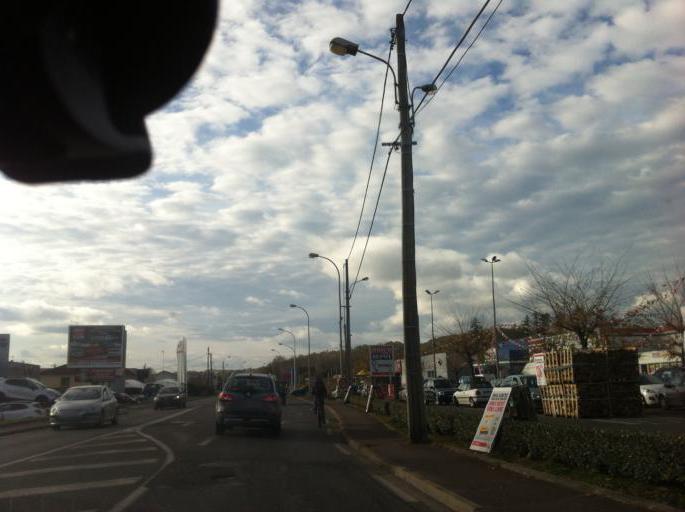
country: FR
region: Aquitaine
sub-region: Departement de la Dordogne
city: Trelissac
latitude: 45.1885
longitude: 0.7594
